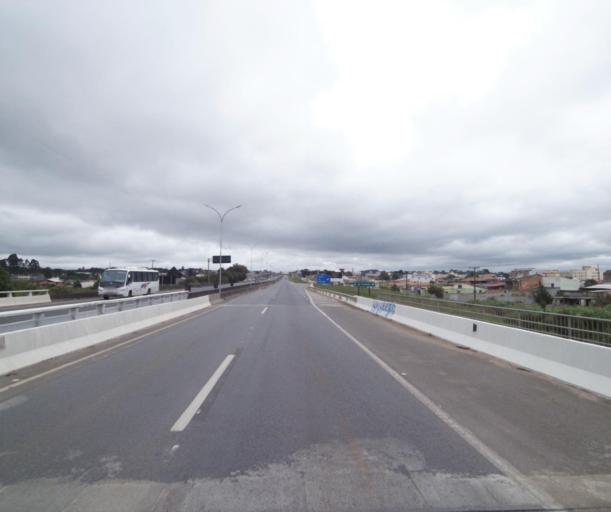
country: BR
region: Parana
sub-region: Quatro Barras
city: Quatro Barras
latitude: -25.3651
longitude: -49.0903
